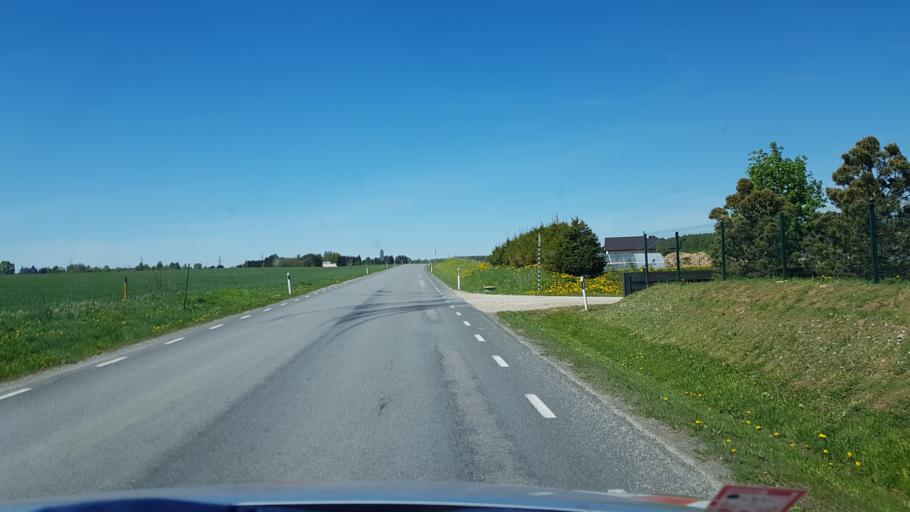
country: EE
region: Tartu
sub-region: UElenurme vald
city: Ulenurme
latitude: 58.3137
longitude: 26.6492
